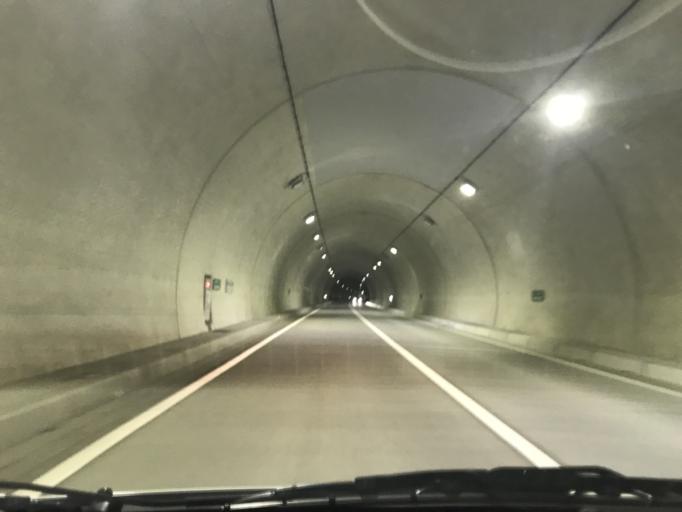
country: JP
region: Iwate
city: Kitakami
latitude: 39.2862
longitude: 141.2405
